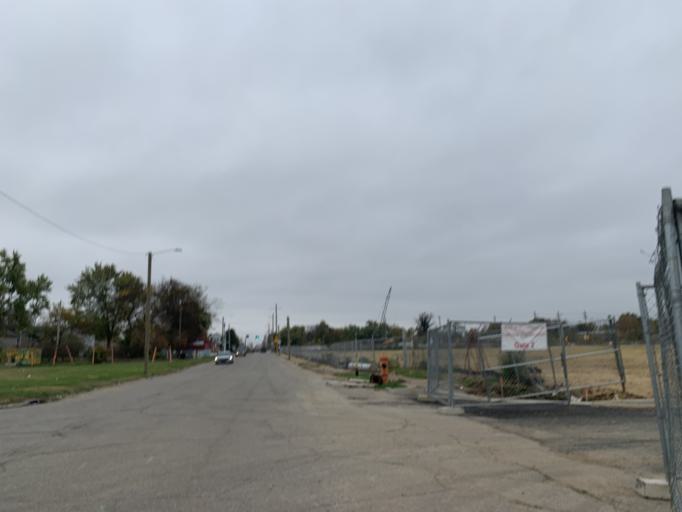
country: US
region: Indiana
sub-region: Floyd County
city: New Albany
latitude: 38.2574
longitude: -85.8003
